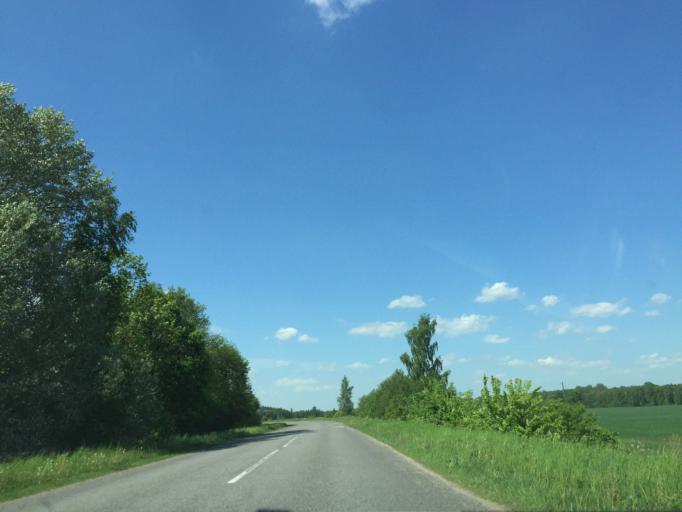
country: LV
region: Rundales
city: Pilsrundale
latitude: 56.5865
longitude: 23.9675
